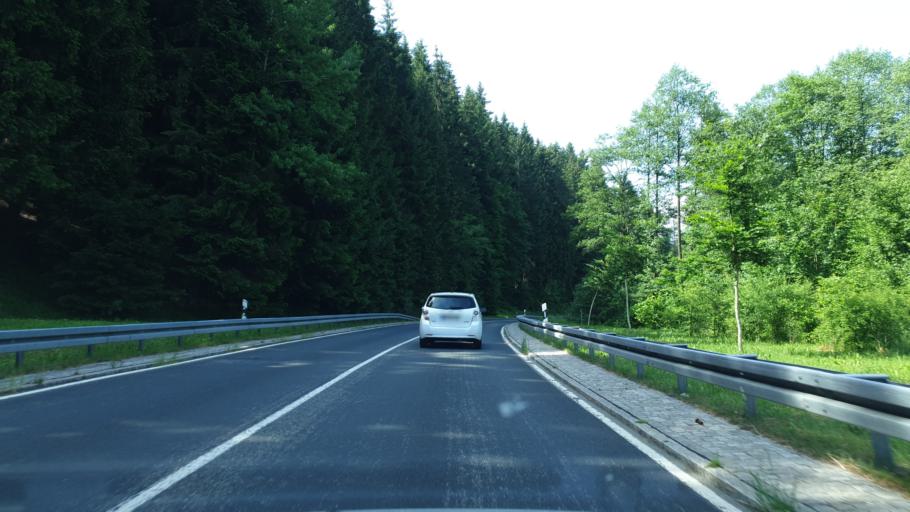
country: DE
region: Saxony
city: Schoenheide
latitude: 50.4971
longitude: 12.5505
